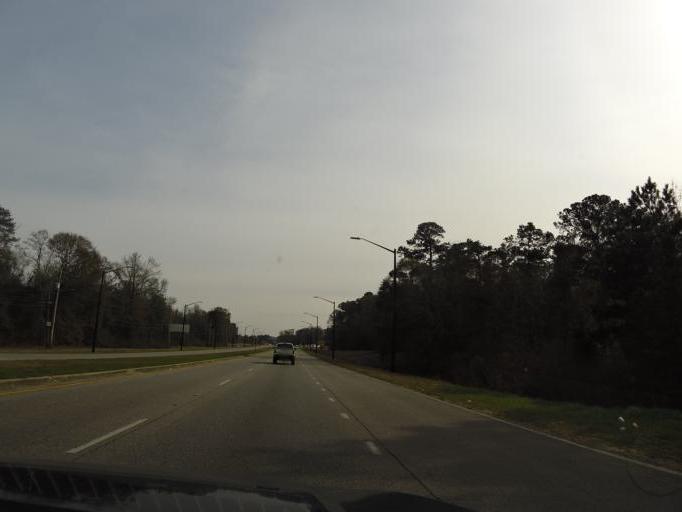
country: US
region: Alabama
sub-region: Houston County
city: Dothan
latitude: 31.2105
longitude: -85.3559
